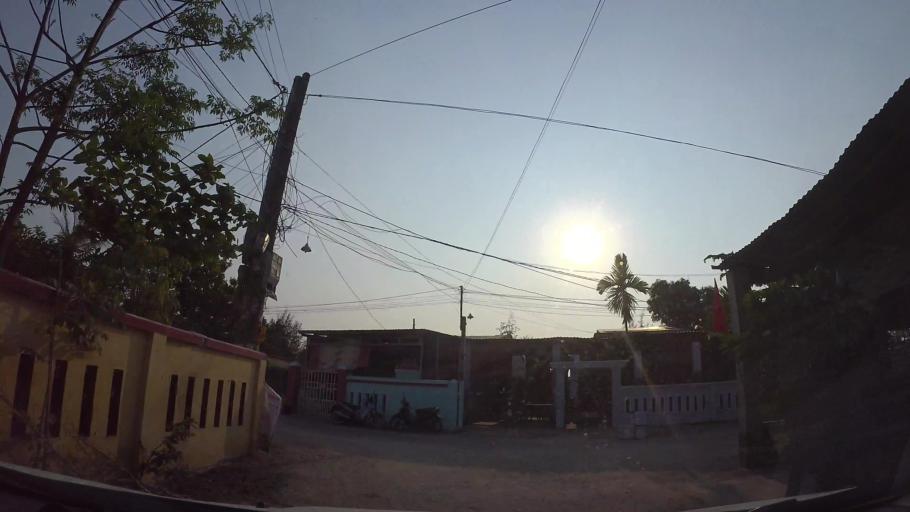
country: VN
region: Da Nang
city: Ngu Hanh Son
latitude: 15.9690
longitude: 108.2446
